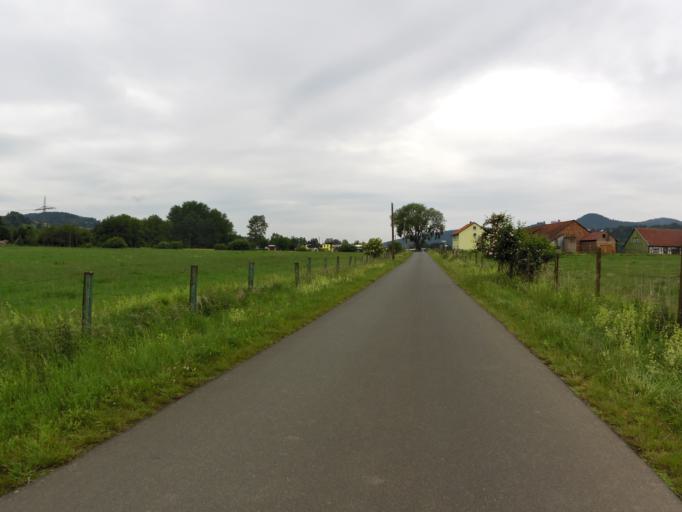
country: DE
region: Hesse
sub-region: Regierungsbezirk Kassel
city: Rotenburg an der Fulda
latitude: 50.9849
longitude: 9.7524
